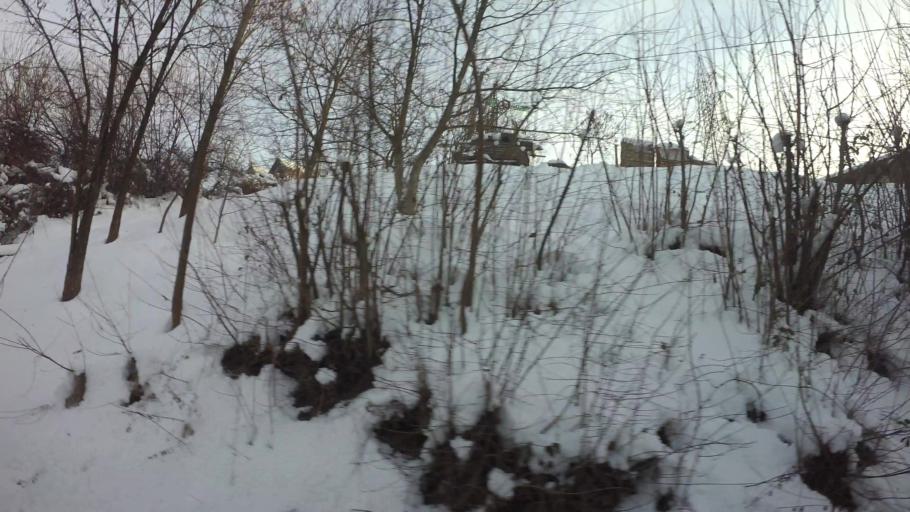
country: BA
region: Federation of Bosnia and Herzegovina
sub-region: Kanton Sarajevo
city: Sarajevo
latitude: 43.8380
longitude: 18.3606
